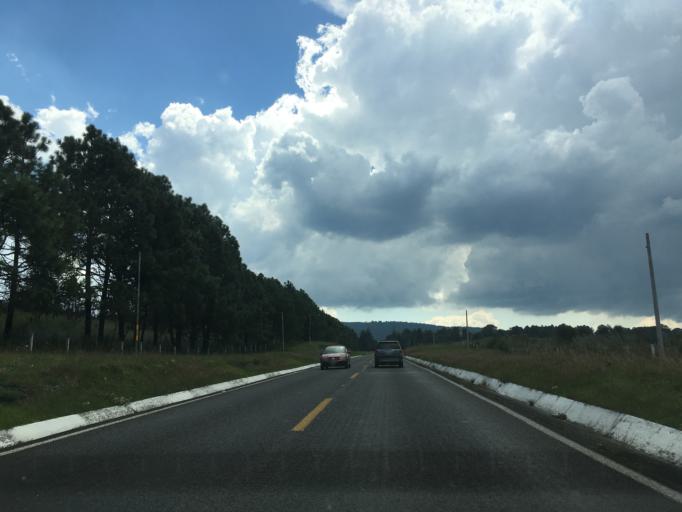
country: MX
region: Michoacan
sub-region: Patzcuaro
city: Santa Ana Chapitiro
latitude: 19.5202
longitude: -101.6635
